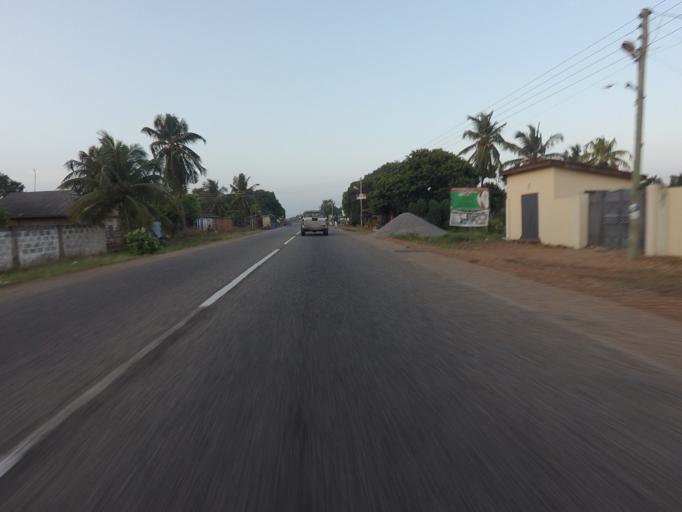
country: GH
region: Volta
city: Anloga
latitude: 5.8253
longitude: 0.9488
